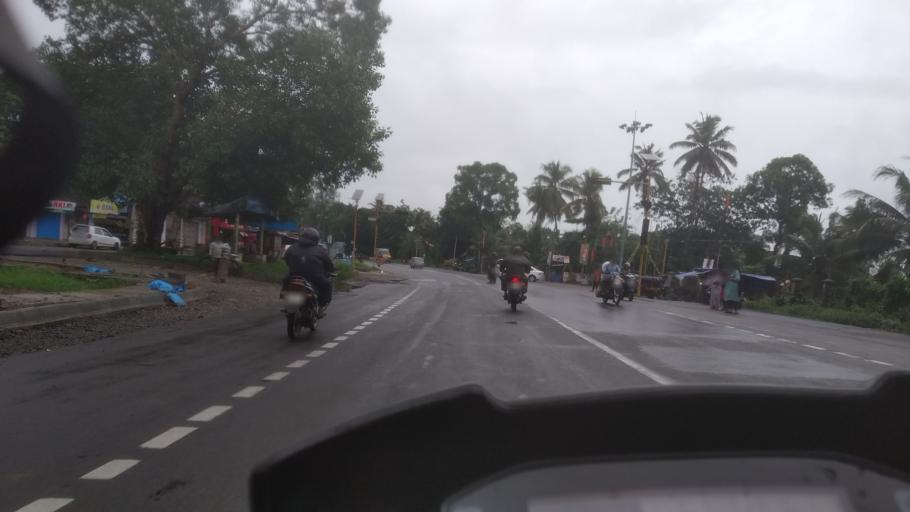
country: IN
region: Kerala
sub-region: Alappuzha
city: Kayankulam
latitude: 9.1503
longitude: 76.5132
